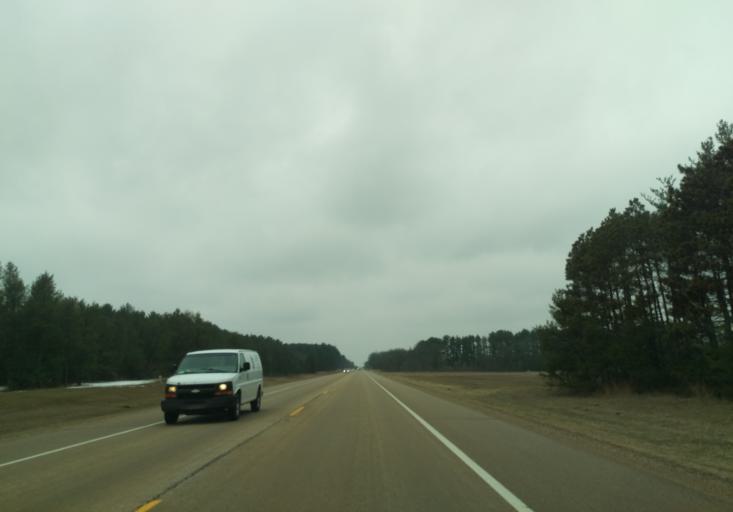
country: US
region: Wisconsin
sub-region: Sauk County
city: Spring Green
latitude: 43.1909
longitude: -90.1609
